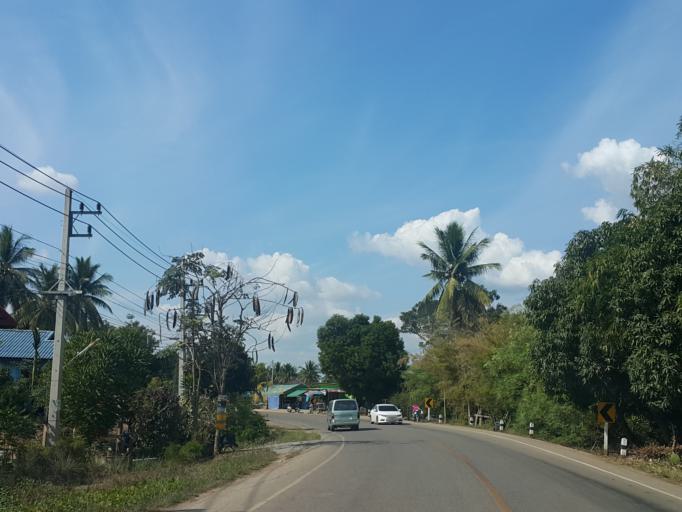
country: TH
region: Sukhothai
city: Sawankhalok
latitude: 17.2921
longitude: 99.8313
